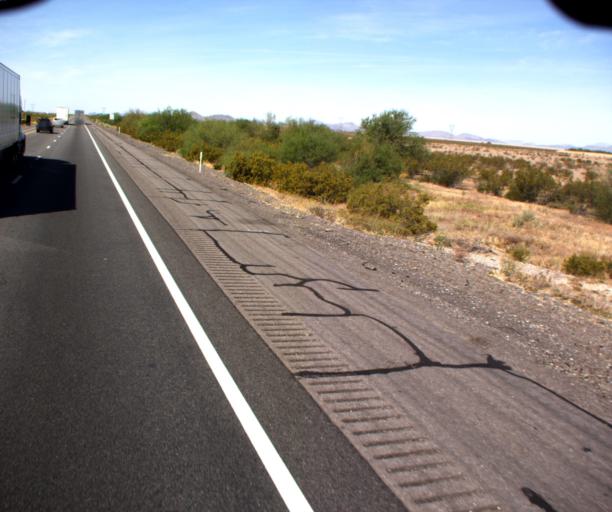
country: US
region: Arizona
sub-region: La Paz County
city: Salome
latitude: 33.5711
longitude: -113.3652
